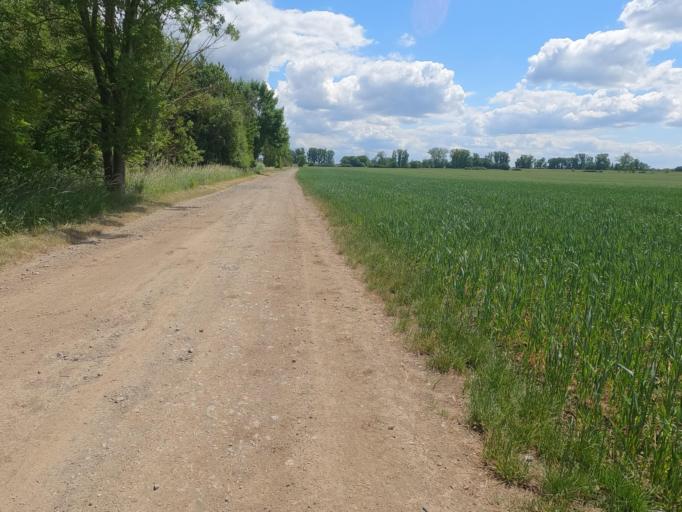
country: DE
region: Rheinland-Pfalz
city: Eich
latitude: 49.7069
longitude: 8.4087
